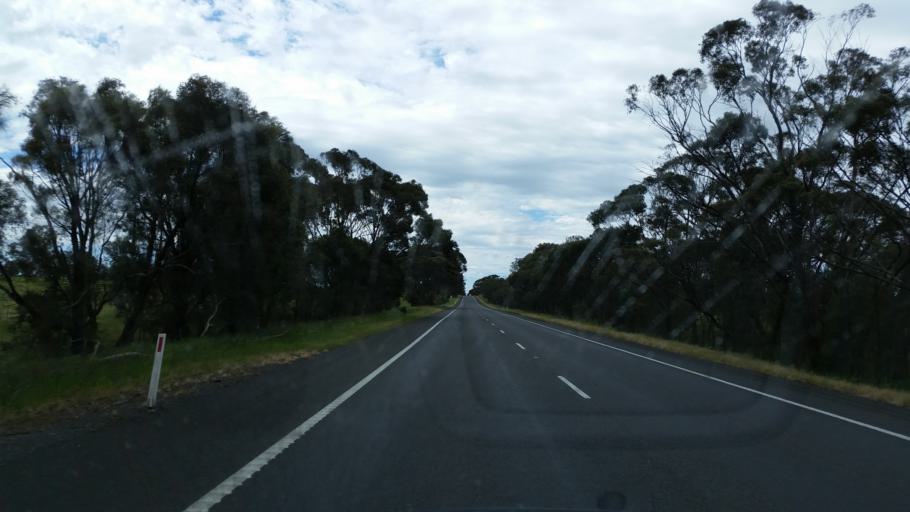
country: AU
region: South Australia
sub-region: Tatiara
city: Bordertown
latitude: -36.3477
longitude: 140.9932
